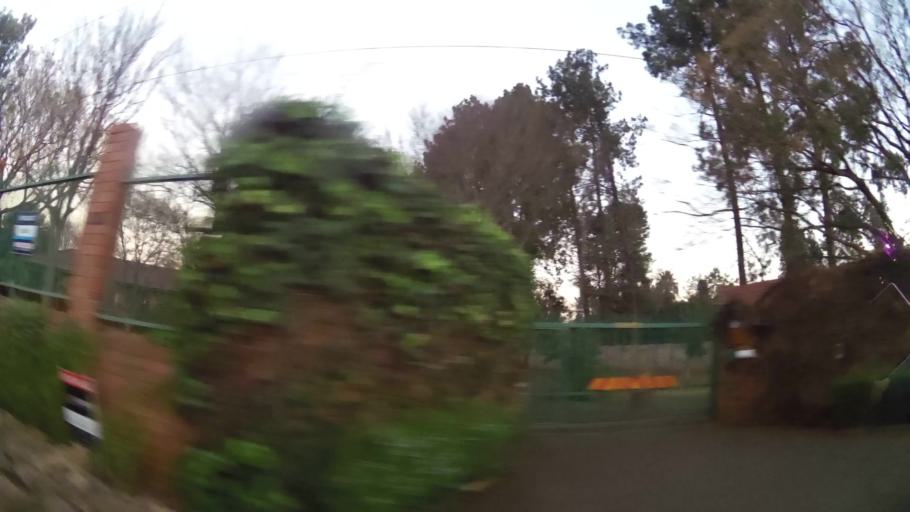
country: ZA
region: Gauteng
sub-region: City of Tshwane Metropolitan Municipality
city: Centurion
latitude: -25.8466
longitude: 28.1182
